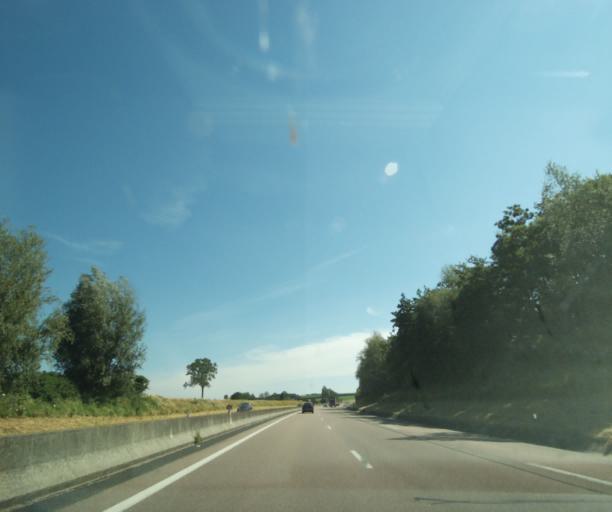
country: FR
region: Lorraine
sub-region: Departement des Vosges
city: Chatenois
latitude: 48.3689
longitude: 5.8712
